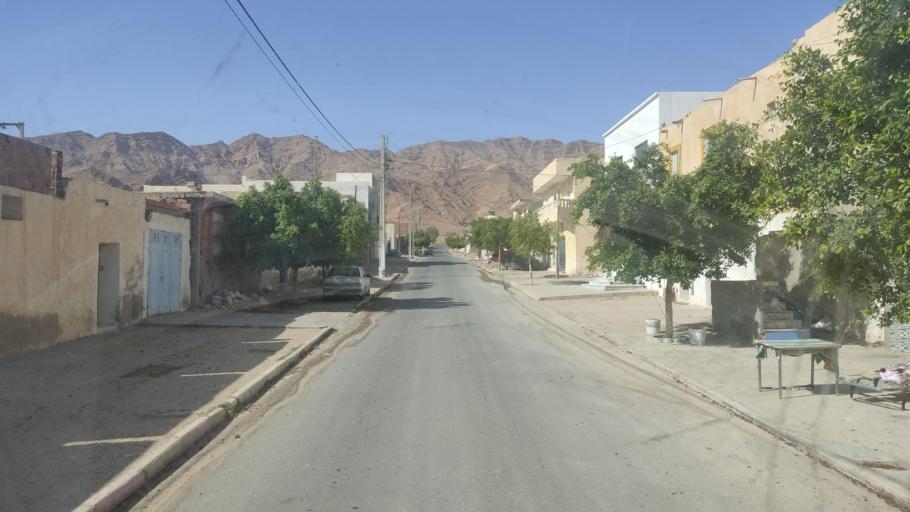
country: TN
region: Gafsa
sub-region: Gafsa Municipality
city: Gafsa
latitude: 34.3378
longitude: 8.9232
